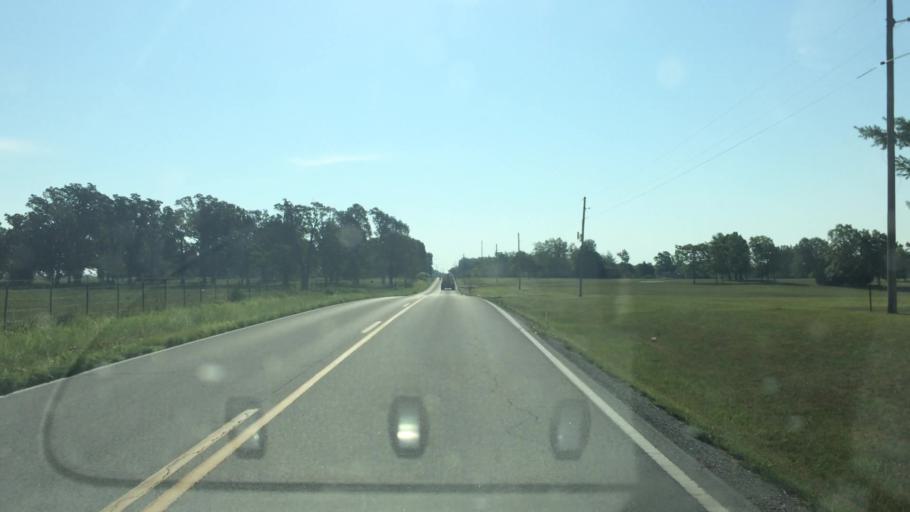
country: US
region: Missouri
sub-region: Greene County
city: Strafford
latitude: 37.2717
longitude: -93.1727
